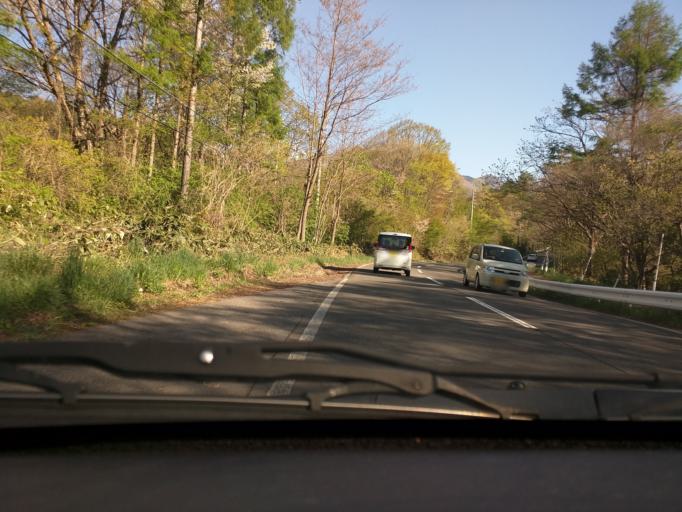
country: JP
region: Nagano
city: Nagano-shi
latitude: 36.6987
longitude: 138.1530
